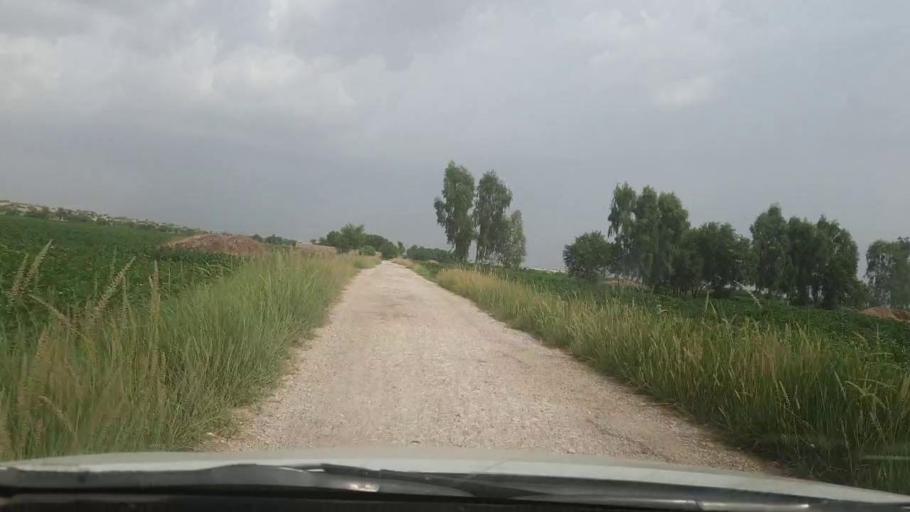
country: PK
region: Sindh
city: Kot Diji
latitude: 27.3376
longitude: 69.0342
